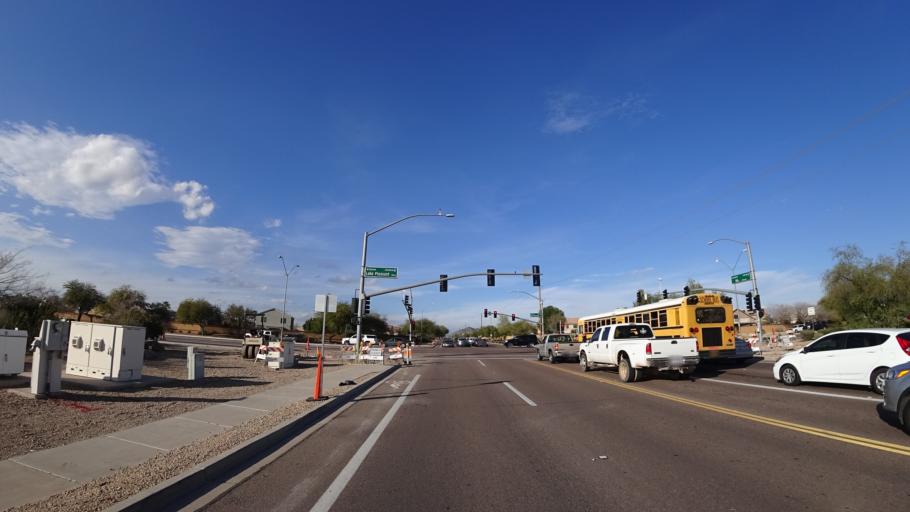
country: US
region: Arizona
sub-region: Maricopa County
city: Sun City
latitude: 33.6742
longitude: -112.2552
